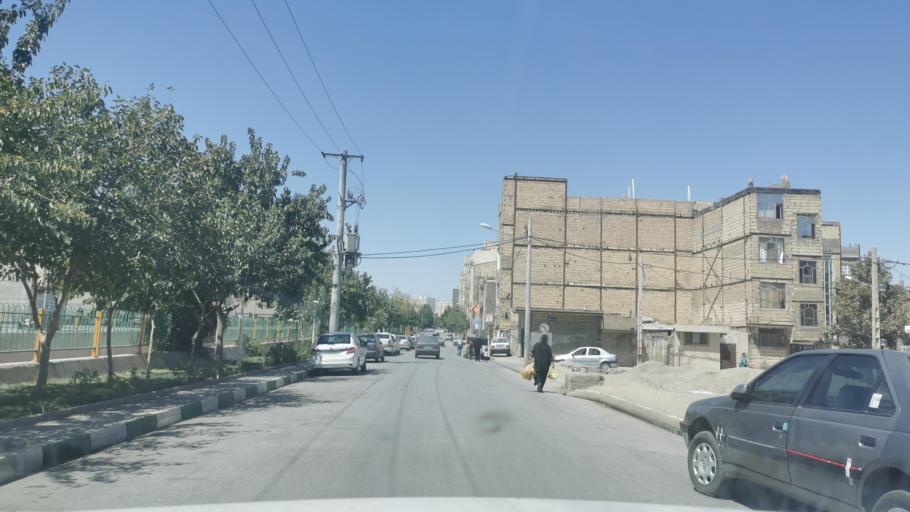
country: IR
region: Razavi Khorasan
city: Mashhad
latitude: 36.3597
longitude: 59.5608
